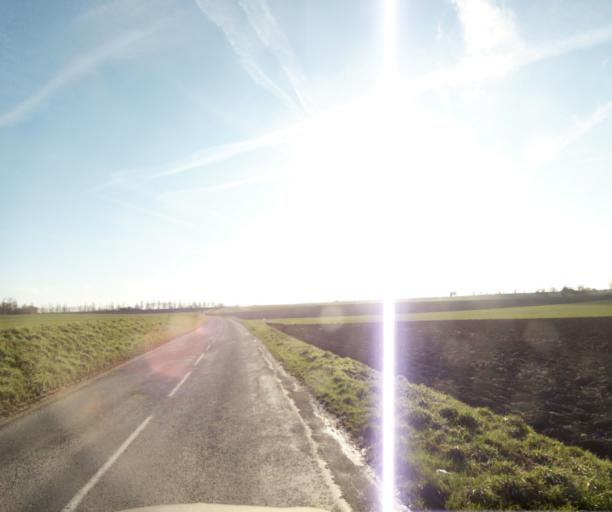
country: FR
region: Nord-Pas-de-Calais
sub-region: Departement du Nord
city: Saultain
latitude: 50.3261
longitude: 3.5745
